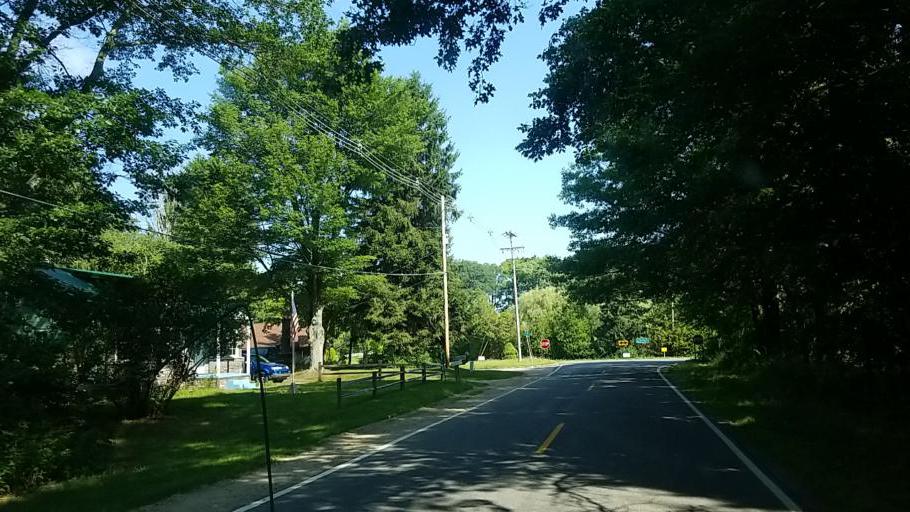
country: US
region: Michigan
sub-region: Muskegon County
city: Montague
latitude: 43.3566
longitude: -86.4104
